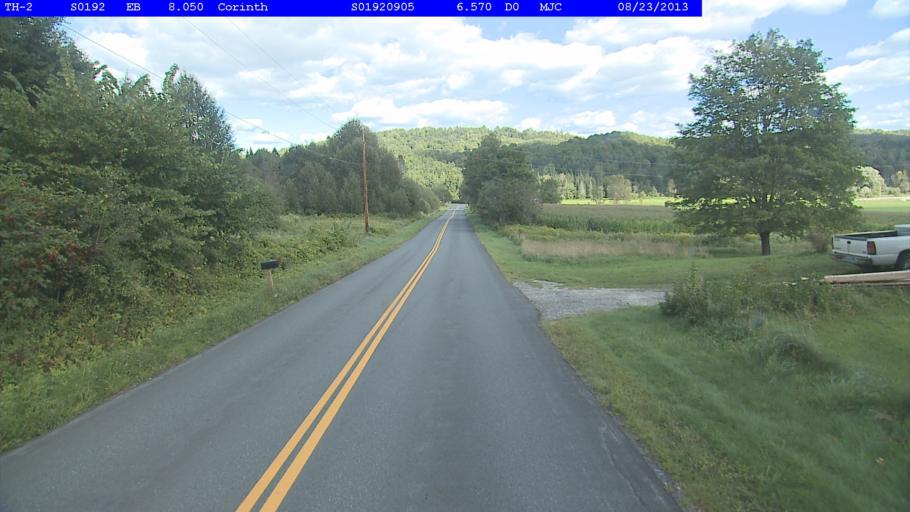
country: US
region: New Hampshire
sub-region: Grafton County
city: Orford
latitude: 44.0091
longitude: -72.2458
